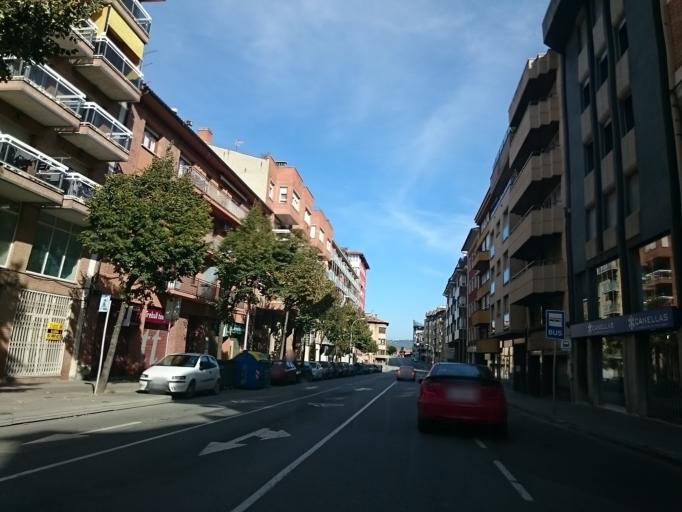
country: ES
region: Catalonia
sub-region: Provincia de Barcelona
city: Vic
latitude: 41.9339
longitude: 2.2537
